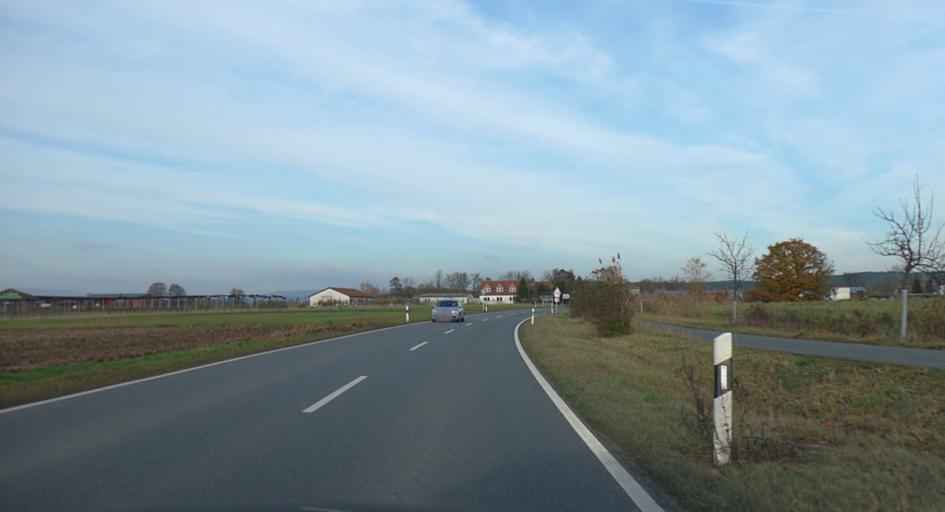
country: DE
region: Bavaria
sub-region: Upper Franconia
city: Poxdorf
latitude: 49.6621
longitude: 11.0608
